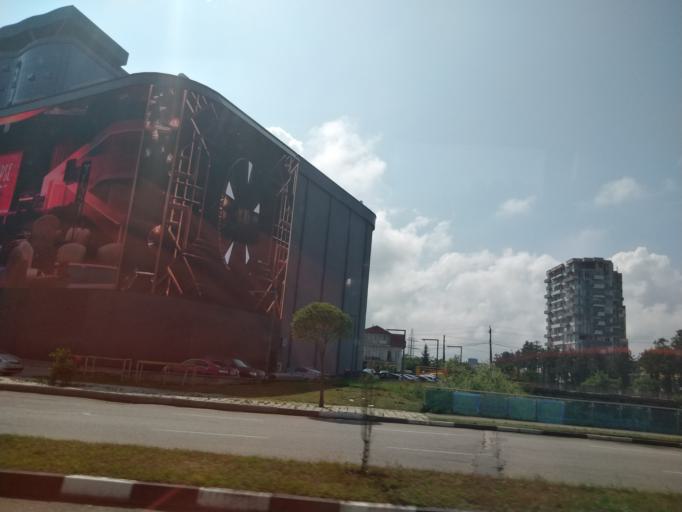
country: GE
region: Ajaria
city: Batumi
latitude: 41.6270
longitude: 41.5997
